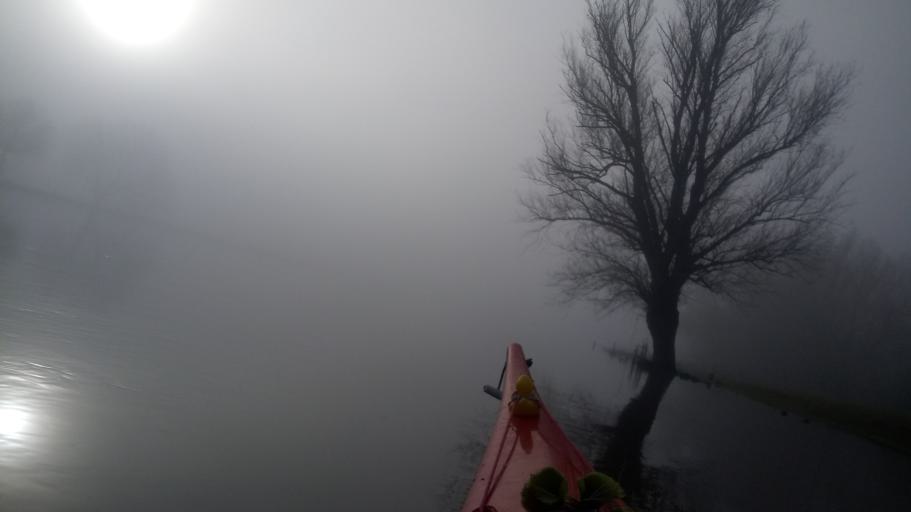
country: NL
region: Gelderland
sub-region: Gemeente Brummen
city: Brummen
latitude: 52.0769
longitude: 6.1680
